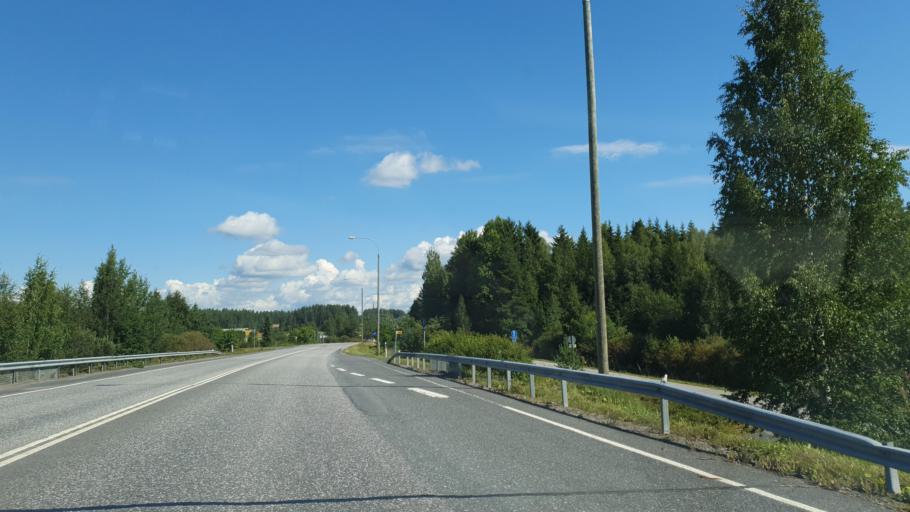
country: FI
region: Northern Savo
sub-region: Ylae-Savo
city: Iisalmi
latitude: 63.6367
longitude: 27.2284
